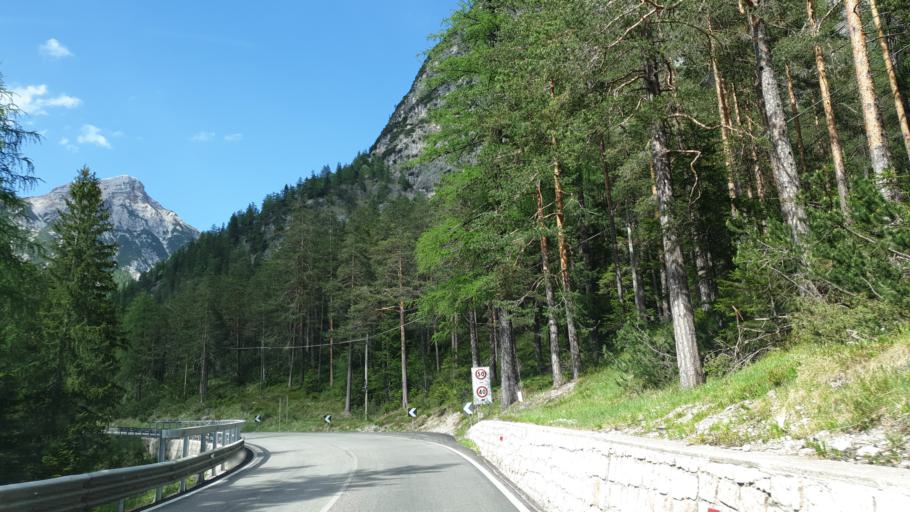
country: IT
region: Veneto
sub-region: Provincia di Belluno
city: Cortina d'Ampezzo
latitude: 46.5882
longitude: 12.1140
